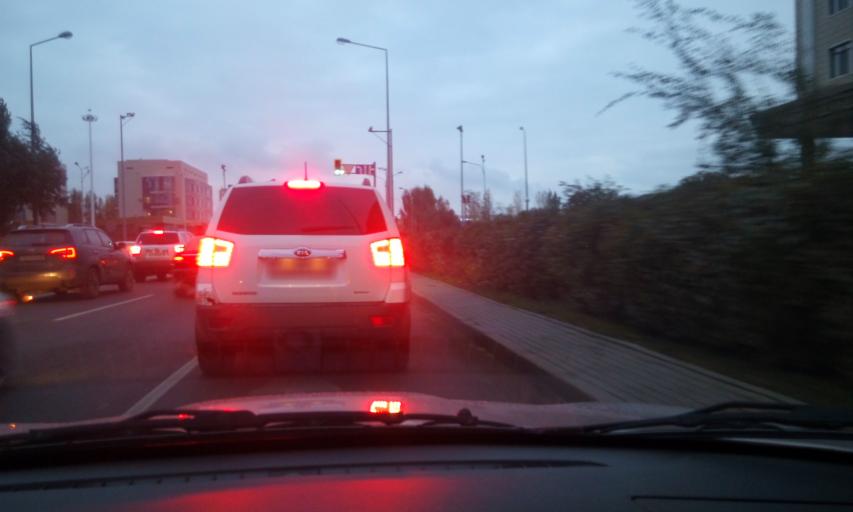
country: KZ
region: Astana Qalasy
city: Astana
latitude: 51.1324
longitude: 71.4341
